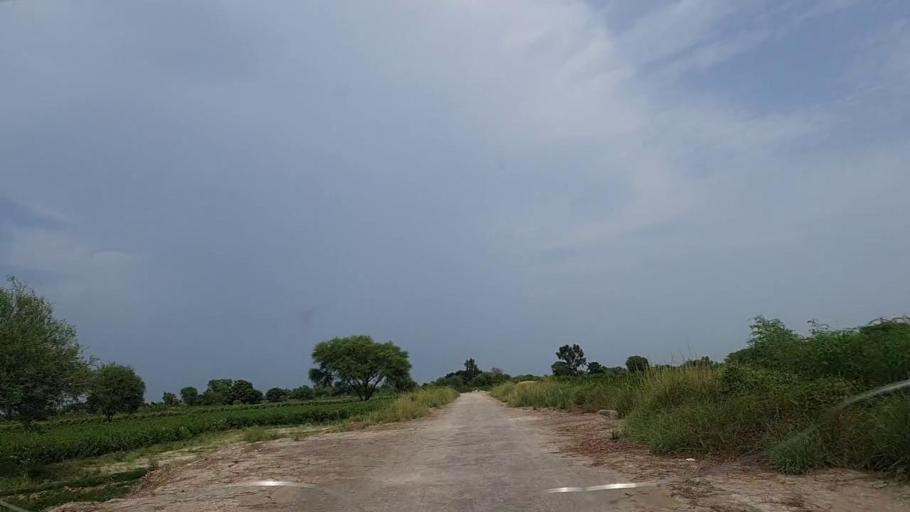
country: PK
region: Sindh
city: Tharu Shah
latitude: 26.8928
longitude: 68.0789
